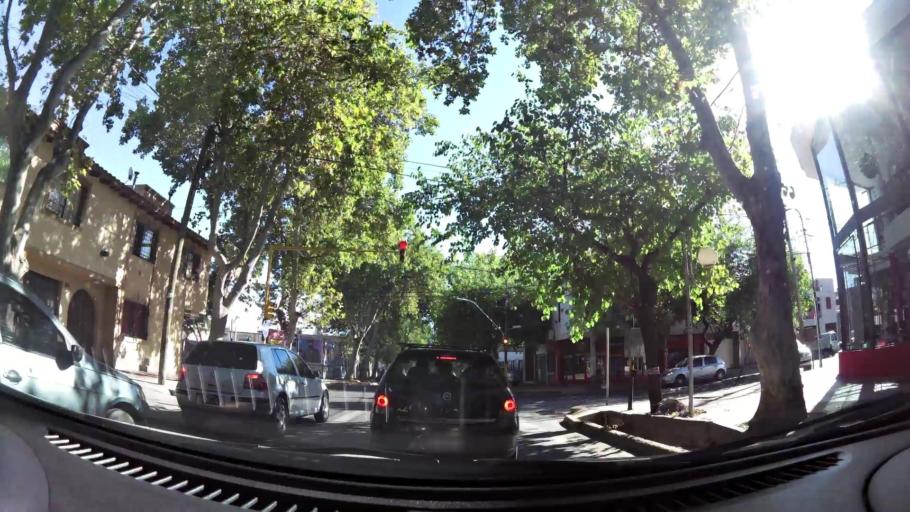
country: AR
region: Mendoza
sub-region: Departamento de Godoy Cruz
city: Godoy Cruz
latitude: -32.9180
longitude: -68.8431
